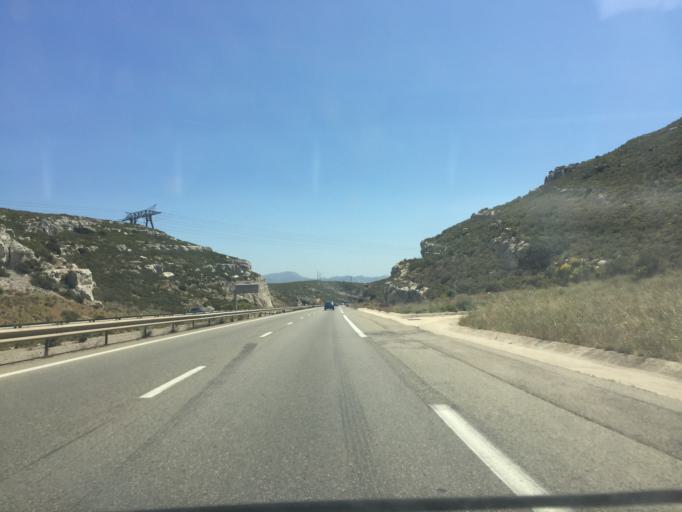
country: FR
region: Provence-Alpes-Cote d'Azur
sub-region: Departement des Bouches-du-Rhone
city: Les Pennes-Mirabeau
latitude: 43.3826
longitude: 5.3141
